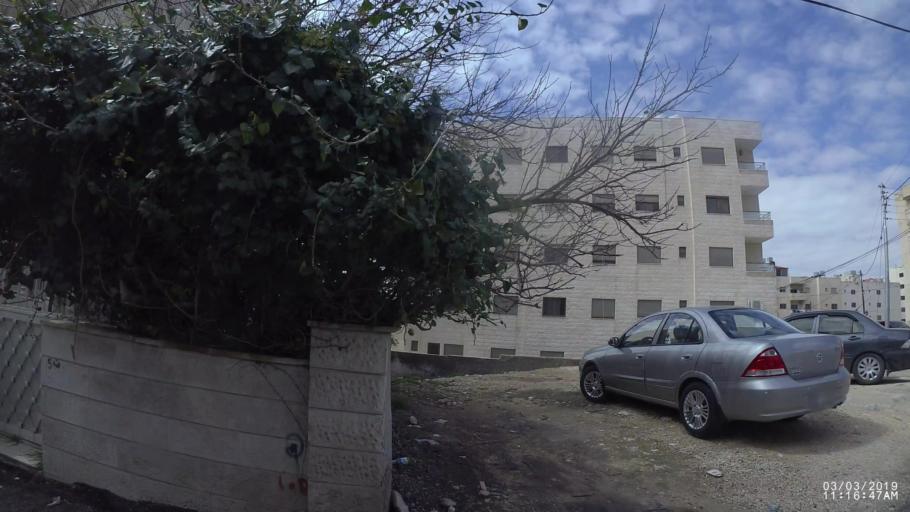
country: JO
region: Amman
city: Amman
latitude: 31.9958
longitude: 35.9139
